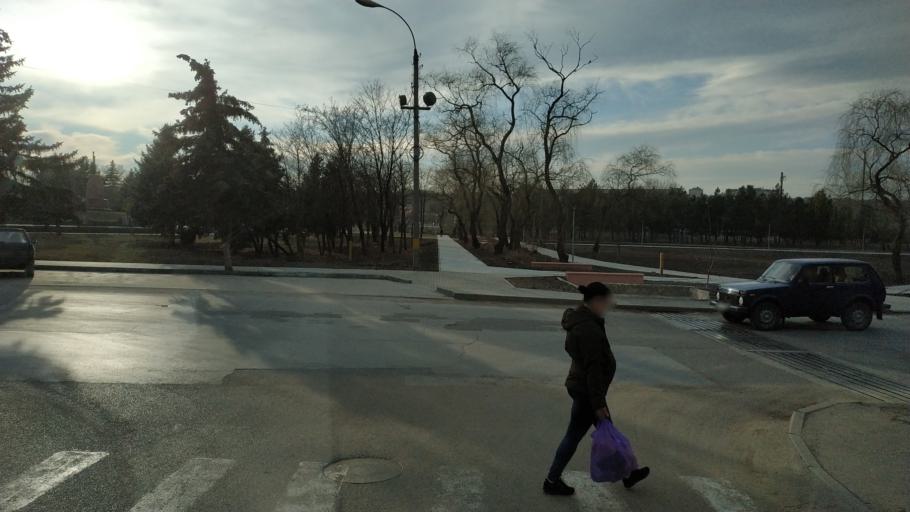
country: MD
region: Nisporeni
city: Nisporeni
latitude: 47.0826
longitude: 28.1827
